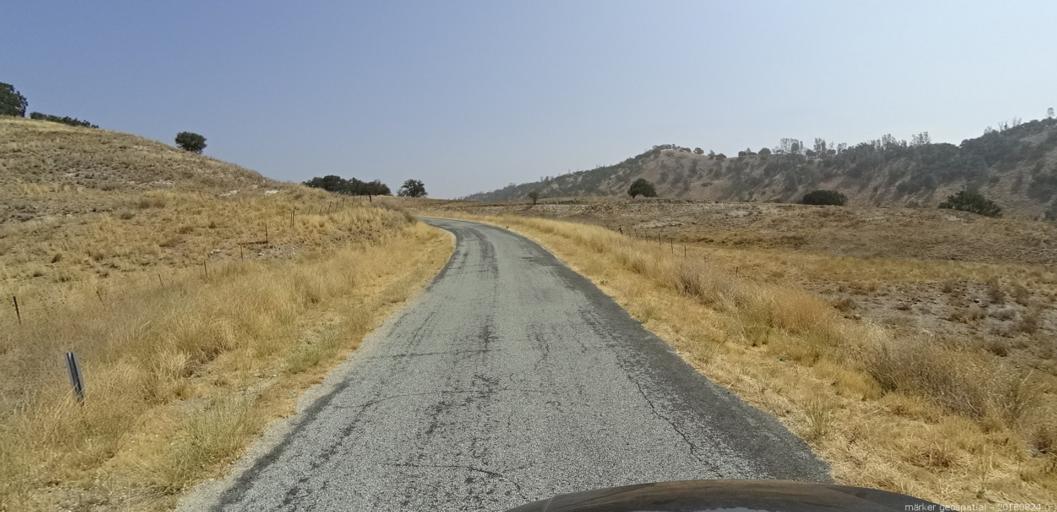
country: US
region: California
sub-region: San Luis Obispo County
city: San Miguel
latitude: 35.9706
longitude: -120.6483
